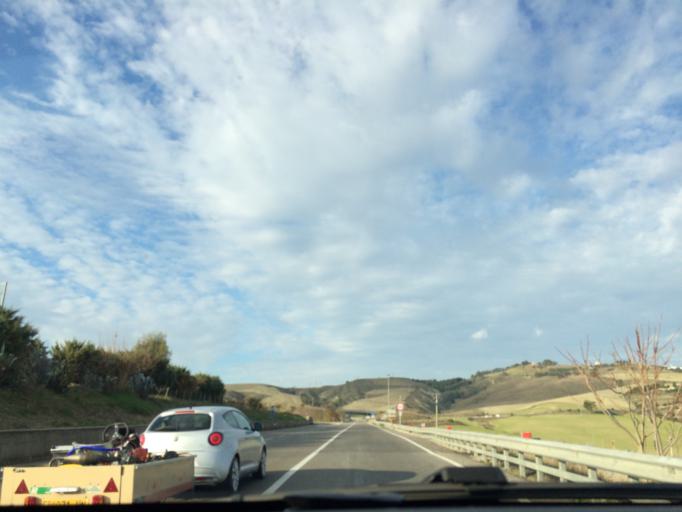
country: IT
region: Basilicate
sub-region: Provincia di Matera
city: Matera
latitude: 40.6411
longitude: 16.5950
